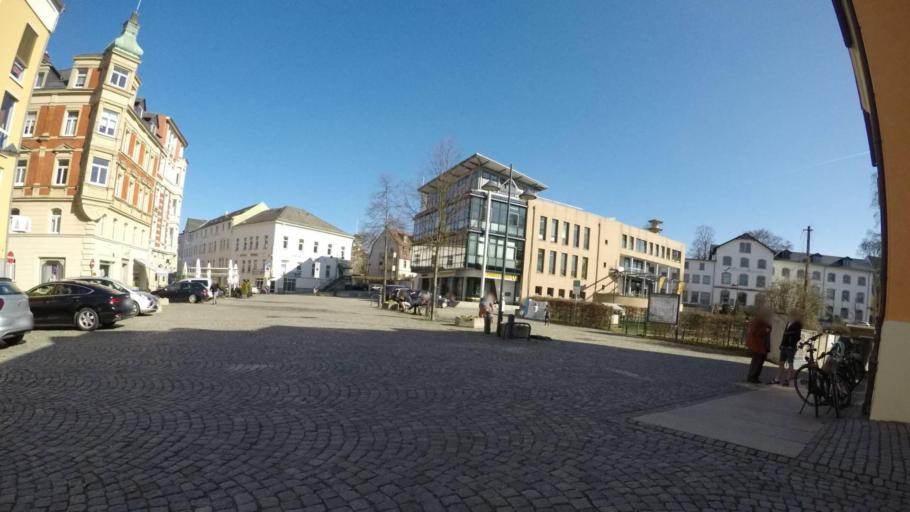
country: DE
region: Saxony
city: Limbach-Oberfrohna
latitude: 50.8588
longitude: 12.7611
